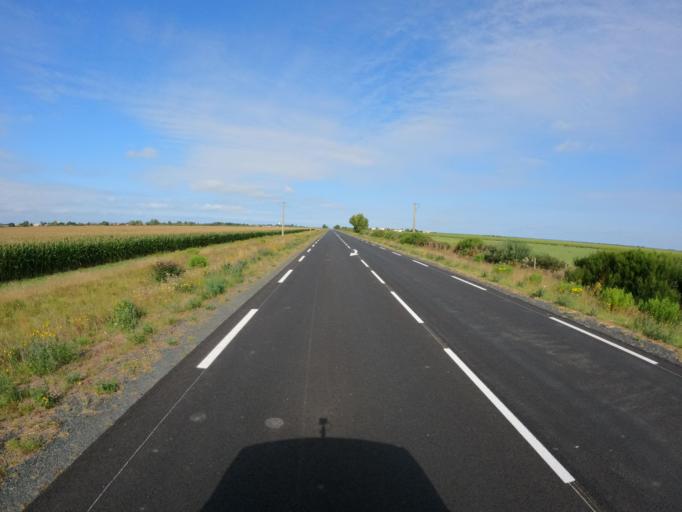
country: FR
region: Pays de la Loire
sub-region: Departement de la Vendee
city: Triaize
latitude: 46.3397
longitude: -1.2883
